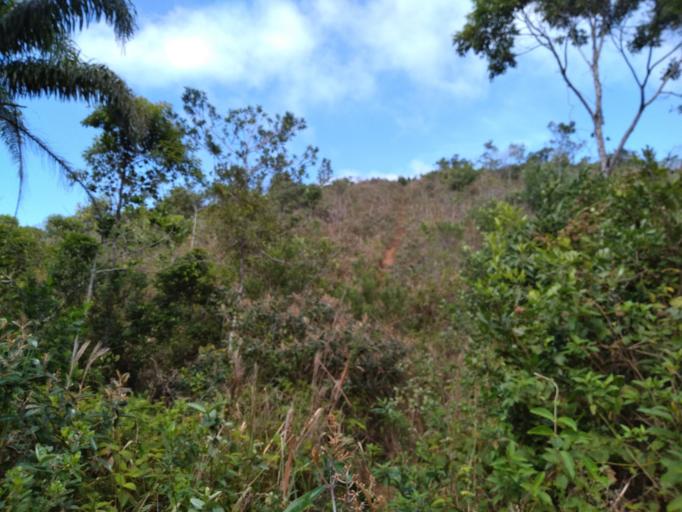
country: BR
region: Sao Paulo
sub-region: Ubatuba
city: Ubatuba
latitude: -23.5393
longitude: -45.1741
